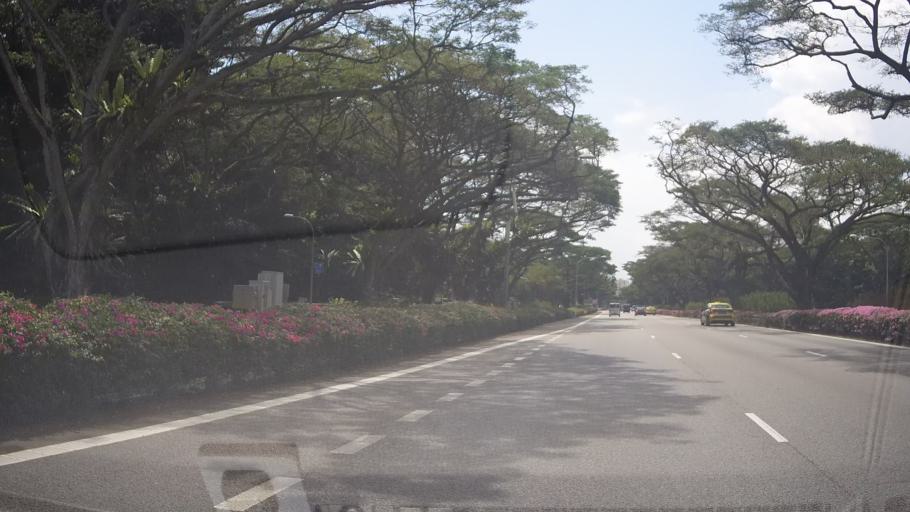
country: SG
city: Singapore
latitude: 1.3101
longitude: 103.9397
